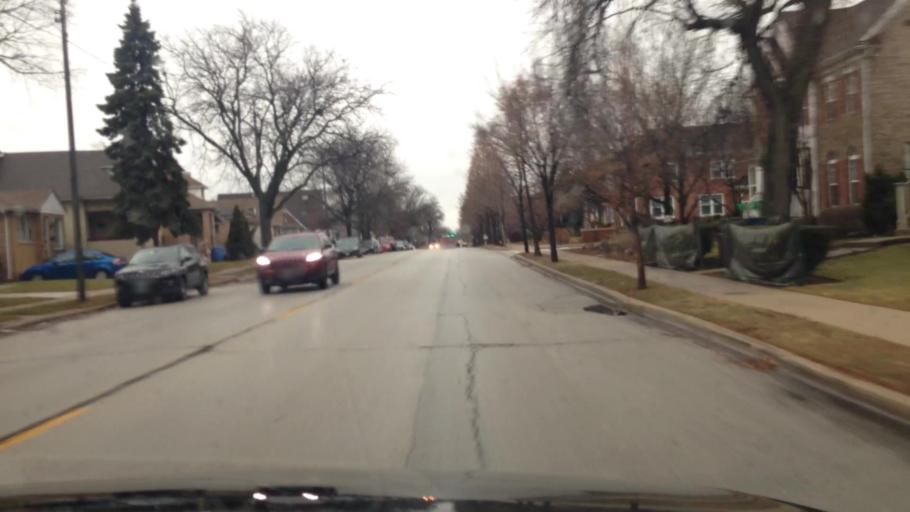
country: US
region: Illinois
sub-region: Cook County
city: Norridge
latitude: 41.9897
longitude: -87.8227
